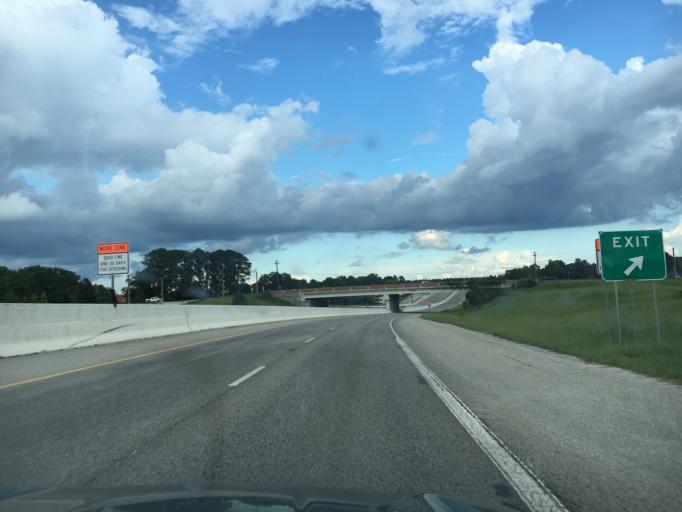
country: US
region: South Carolina
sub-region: Spartanburg County
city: Southern Shops
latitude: 34.9969
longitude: -81.9800
